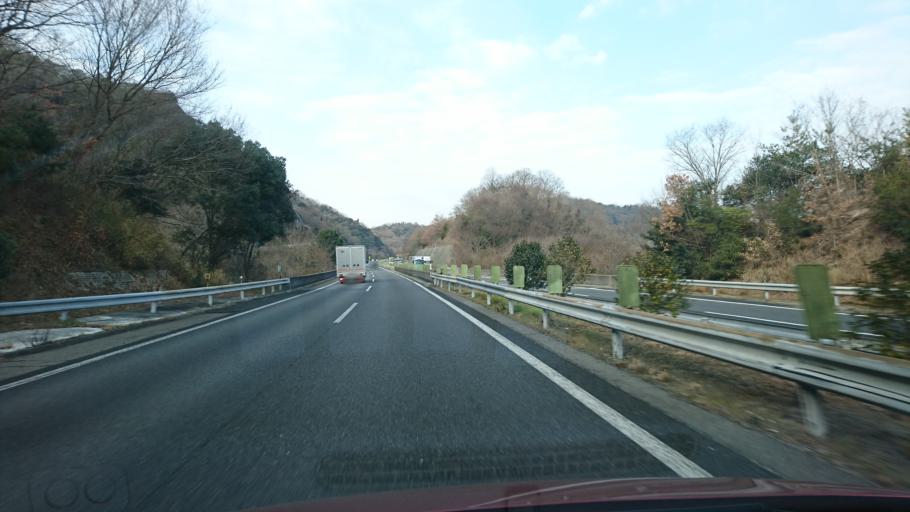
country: JP
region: Hyogo
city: Kariya
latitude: 34.7955
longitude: 134.2035
